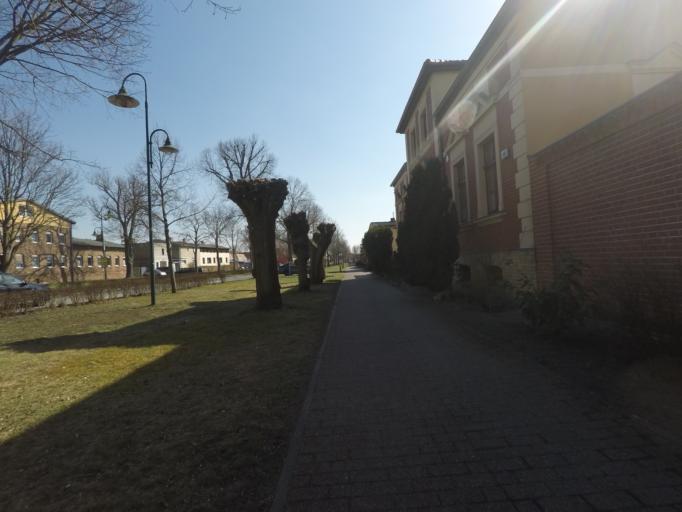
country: DE
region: Brandenburg
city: Britz
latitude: 52.8655
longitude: 13.7489
